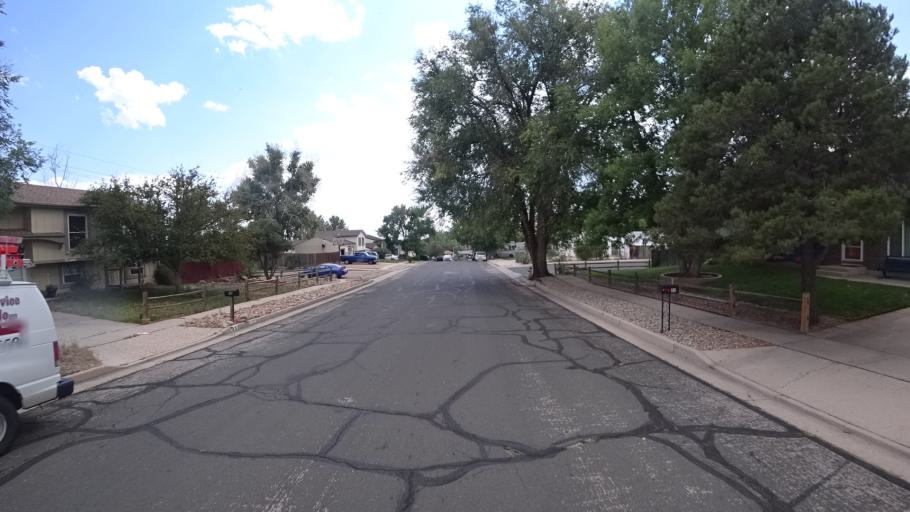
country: US
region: Colorado
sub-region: El Paso County
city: Cimarron Hills
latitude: 38.8312
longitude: -104.7392
